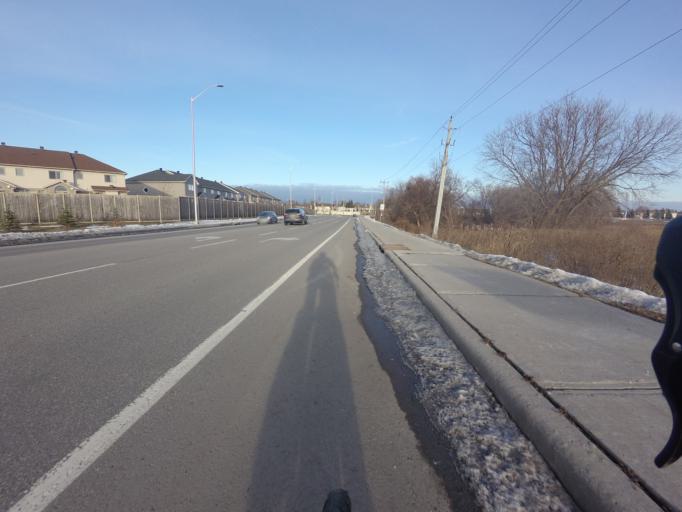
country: CA
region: Ontario
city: Bells Corners
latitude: 45.2773
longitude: -75.8644
